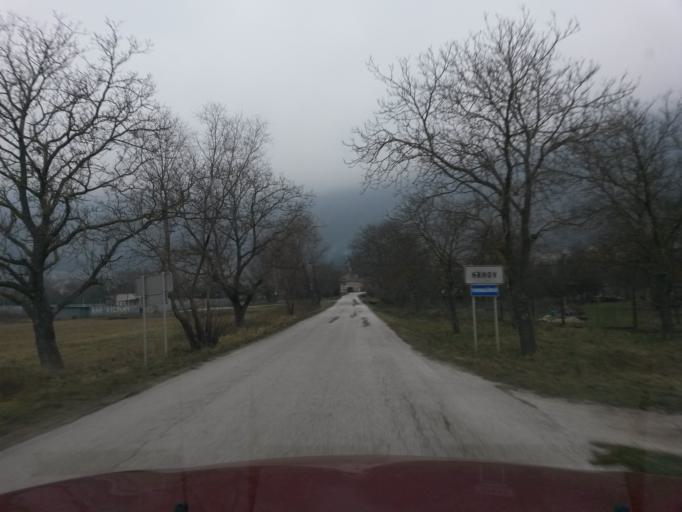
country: SK
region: Kosicky
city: Medzev
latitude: 48.6033
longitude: 20.7573
